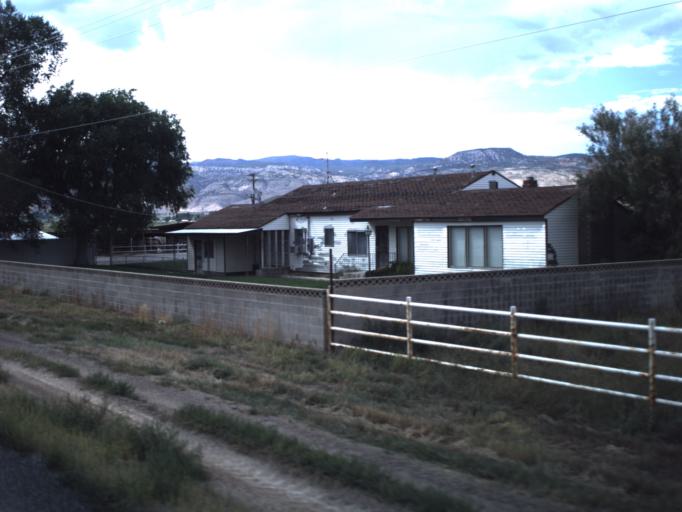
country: US
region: Utah
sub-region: Sevier County
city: Richfield
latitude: 38.7736
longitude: -112.0347
